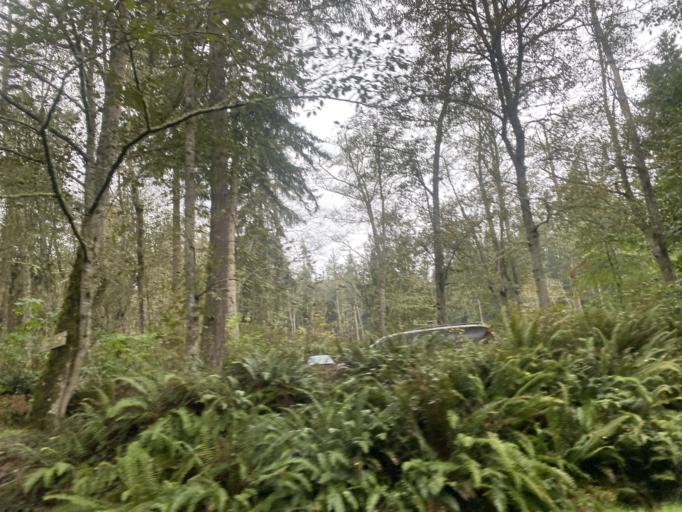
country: US
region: Washington
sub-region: Island County
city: Freeland
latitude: 48.0795
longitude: -122.5612
